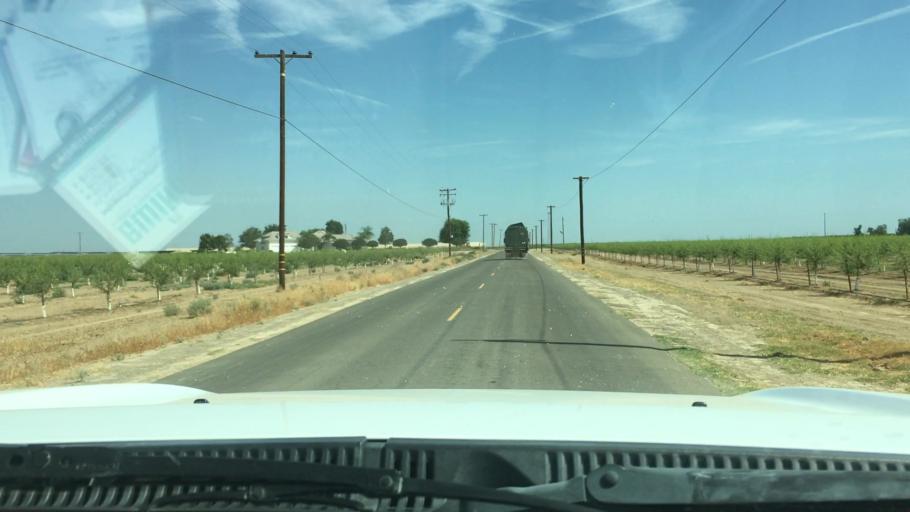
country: US
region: California
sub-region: Kern County
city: Shafter
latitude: 35.4607
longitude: -119.3681
